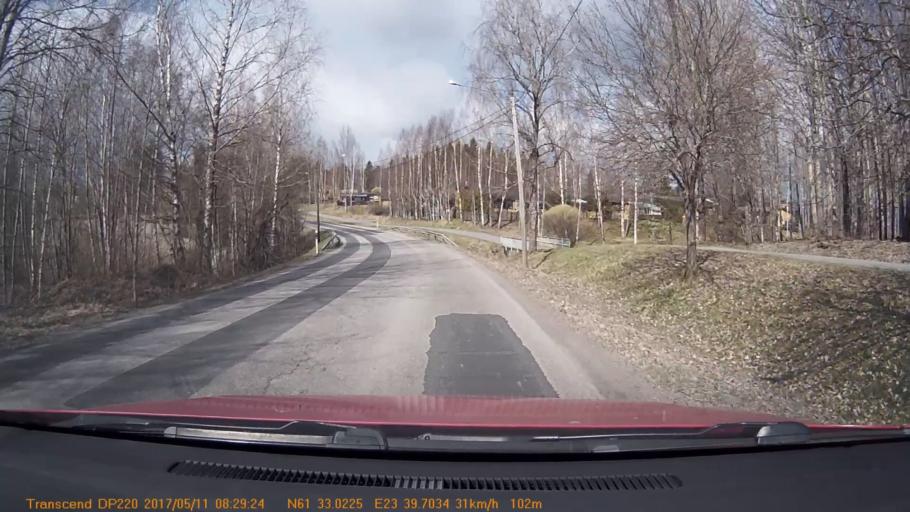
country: FI
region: Pirkanmaa
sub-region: Tampere
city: Yloejaervi
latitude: 61.5504
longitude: 23.6619
